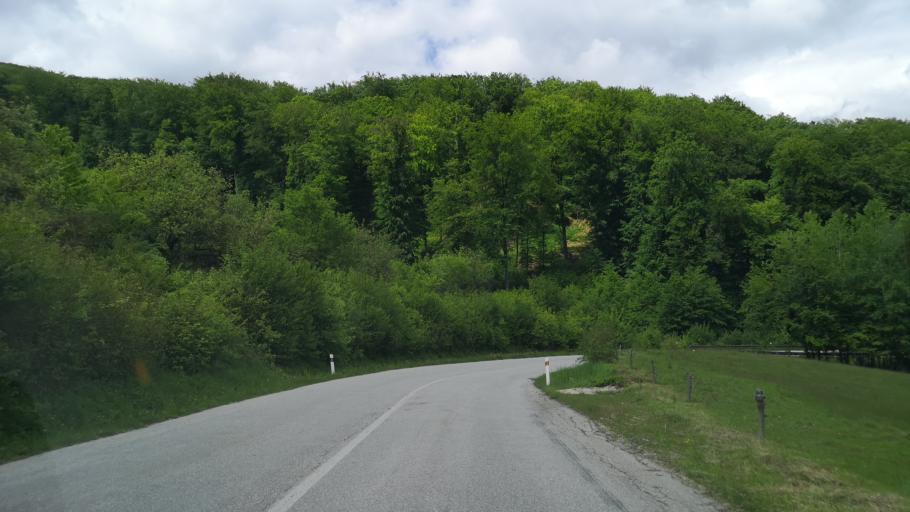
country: SK
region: Kosicky
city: Dobsina
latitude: 48.6419
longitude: 20.3571
